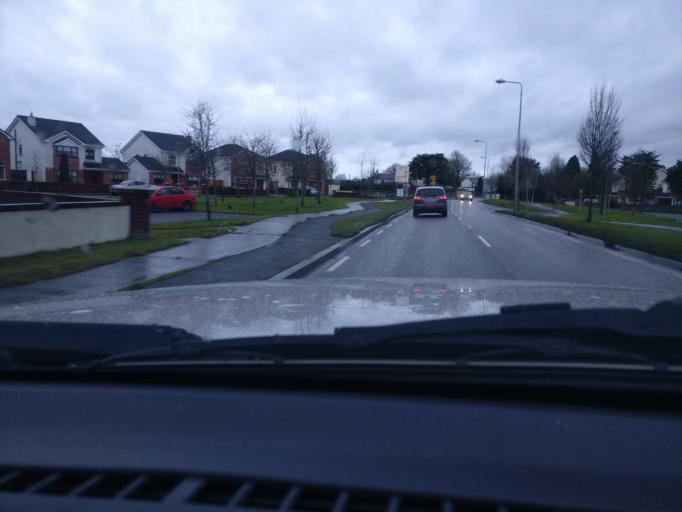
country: IE
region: Leinster
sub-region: An Mhi
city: Longwood
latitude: 53.4567
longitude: -6.9220
